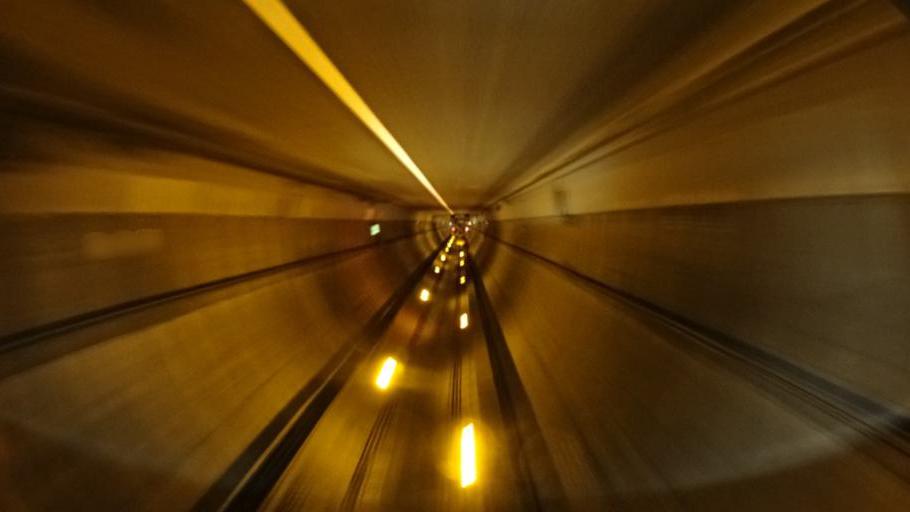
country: JP
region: Gunma
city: Nakanojomachi
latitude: 36.7645
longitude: 138.8230
